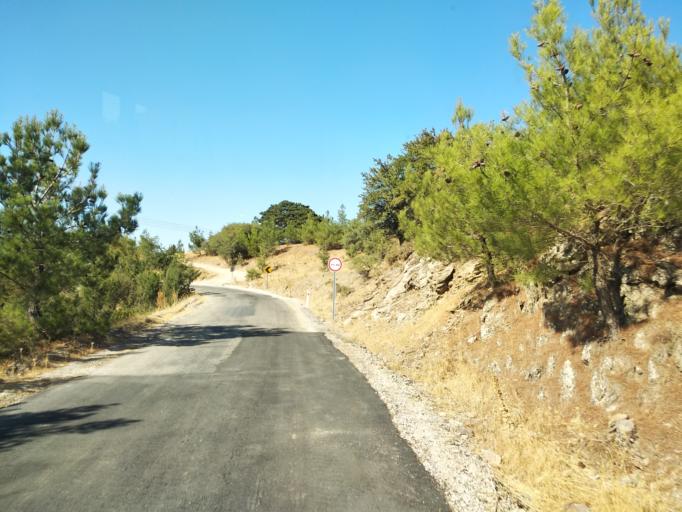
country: TR
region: Izmir
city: Gaziemir
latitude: 38.3107
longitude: 26.9999
